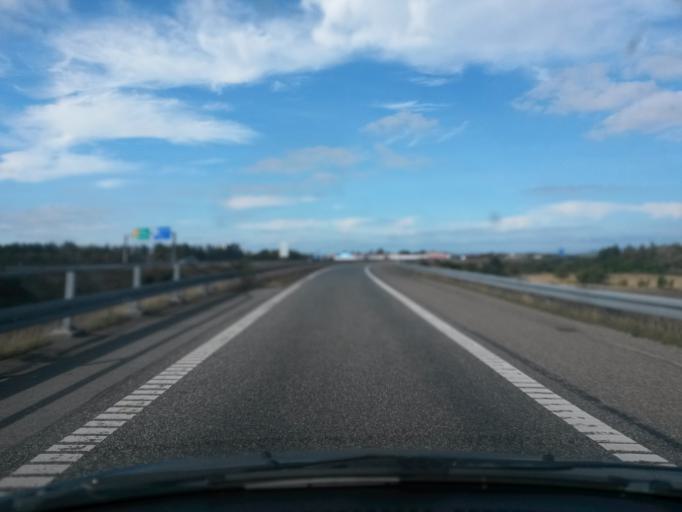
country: DK
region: Central Jutland
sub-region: Herning Kommune
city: Gjellerup Kirkeby
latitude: 56.1275
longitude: 9.0142
